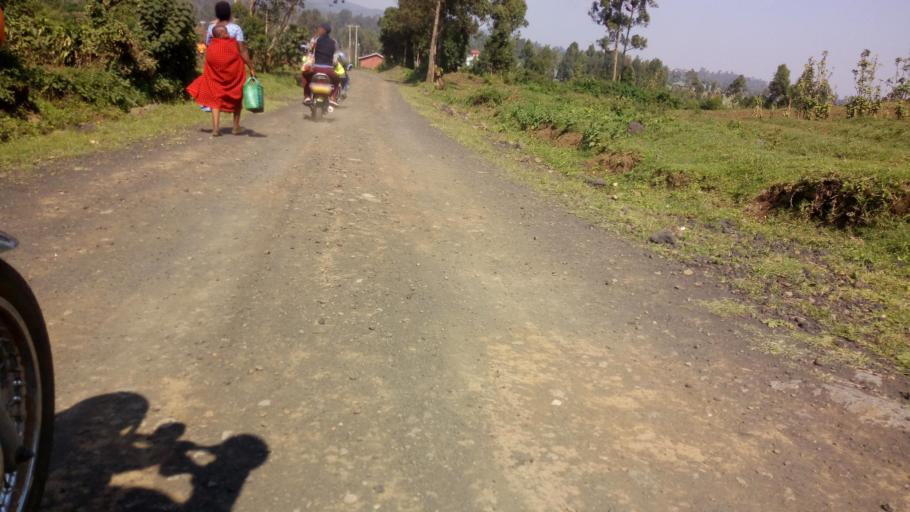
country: UG
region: Western Region
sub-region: Kisoro District
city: Kisoro
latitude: -1.3410
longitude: 29.6315
